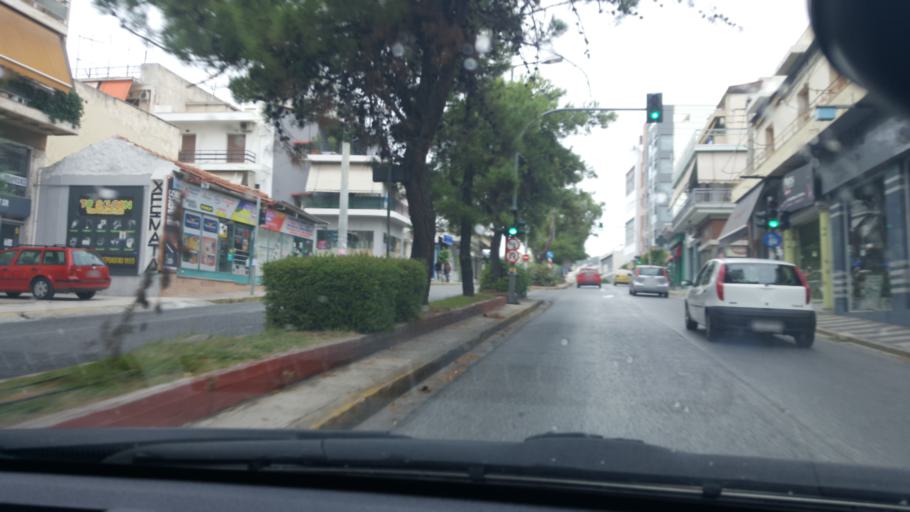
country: GR
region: Attica
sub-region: Nomarchia Athinas
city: Neo Psychiko
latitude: 37.9954
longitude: 23.7729
